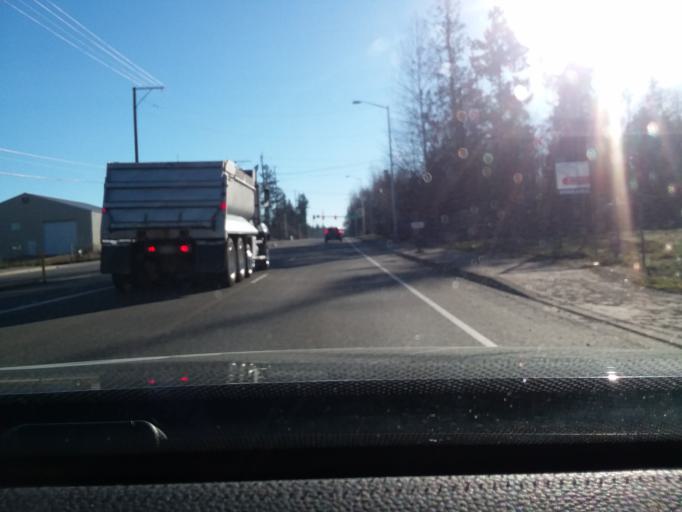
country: US
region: Washington
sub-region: Pierce County
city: Frederickson
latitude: 47.0964
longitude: -122.3475
